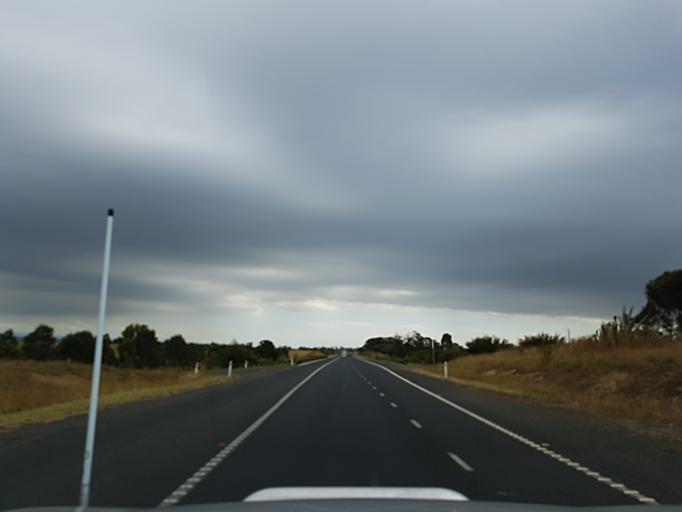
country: AU
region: Victoria
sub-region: Wellington
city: Heyfield
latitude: -38.1295
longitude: 146.8299
